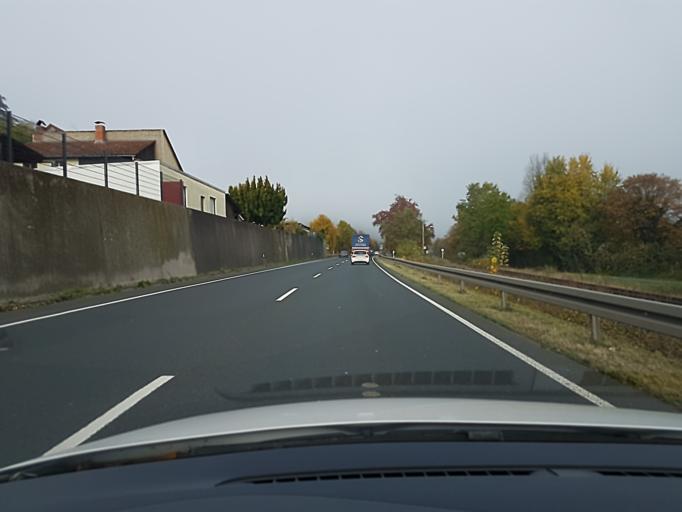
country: DE
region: Bavaria
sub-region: Regierungsbezirk Unterfranken
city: Laudenbach
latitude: 49.7407
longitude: 9.1800
